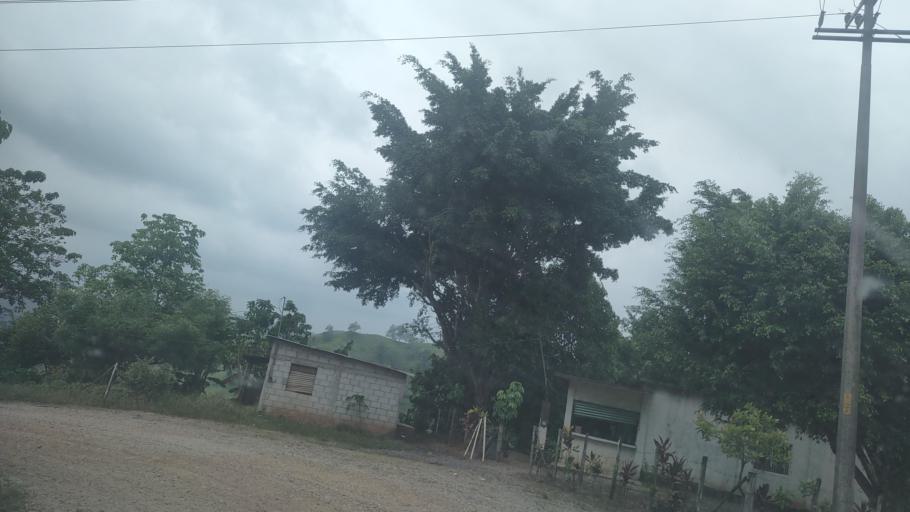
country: MX
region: Tabasco
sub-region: Huimanguillo
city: Francisco Rueda
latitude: 17.4404
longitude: -94.0251
